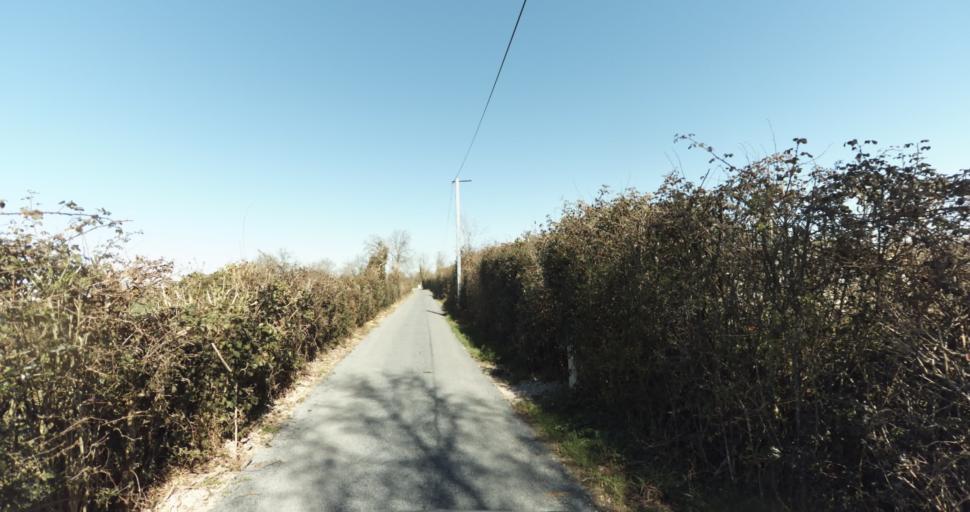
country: FR
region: Lower Normandy
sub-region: Departement du Calvados
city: Livarot
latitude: 48.9781
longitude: 0.0874
